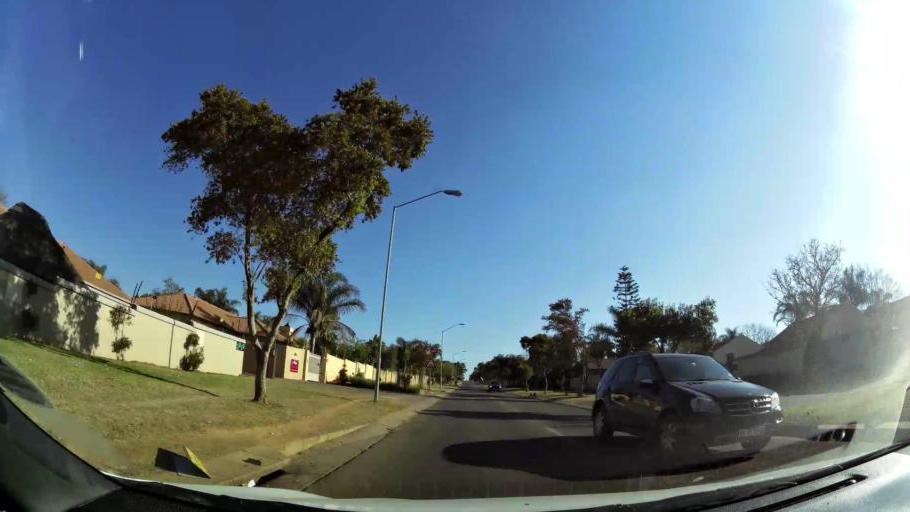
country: ZA
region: Gauteng
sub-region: City of Tshwane Metropolitan Municipality
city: Centurion
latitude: -25.8349
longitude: 28.2984
